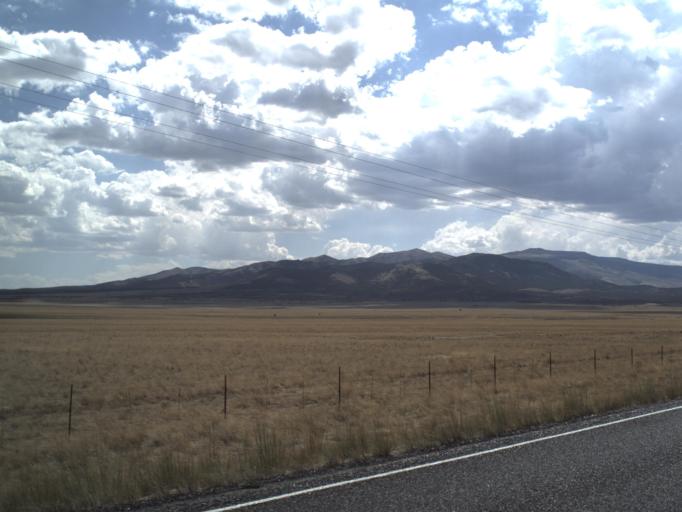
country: US
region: Idaho
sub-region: Power County
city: American Falls
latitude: 41.9684
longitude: -113.0990
